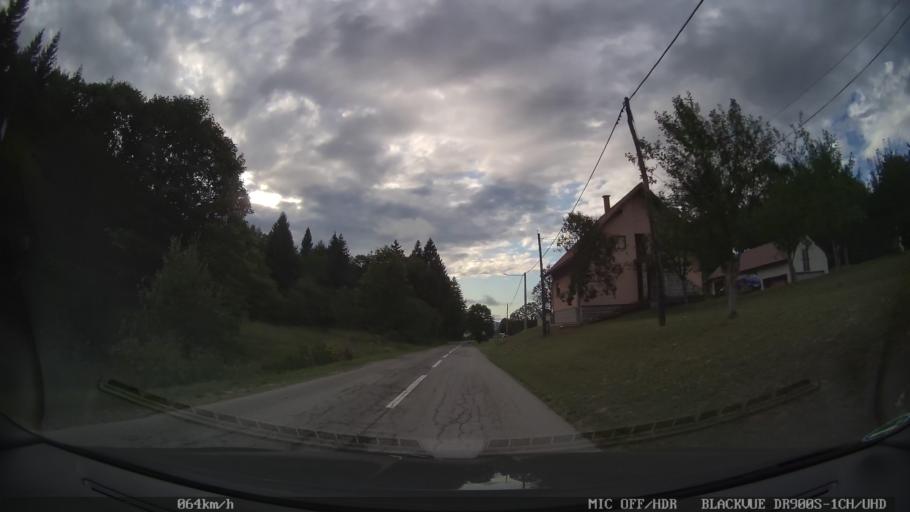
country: HR
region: Licko-Senjska
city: Jezerce
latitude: 44.9638
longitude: 15.5245
